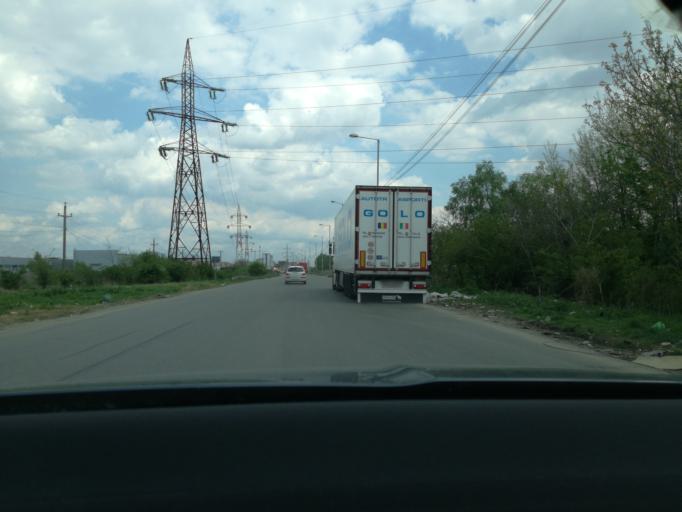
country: RO
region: Ilfov
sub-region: Comuna Chiajna
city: Chiajna
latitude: 44.4407
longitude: 25.9623
